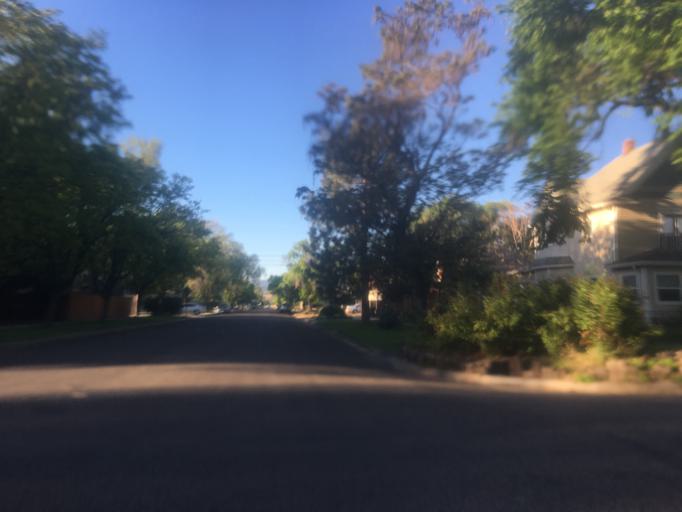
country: US
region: Colorado
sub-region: Mesa County
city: Grand Junction
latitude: 39.0734
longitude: -108.5627
